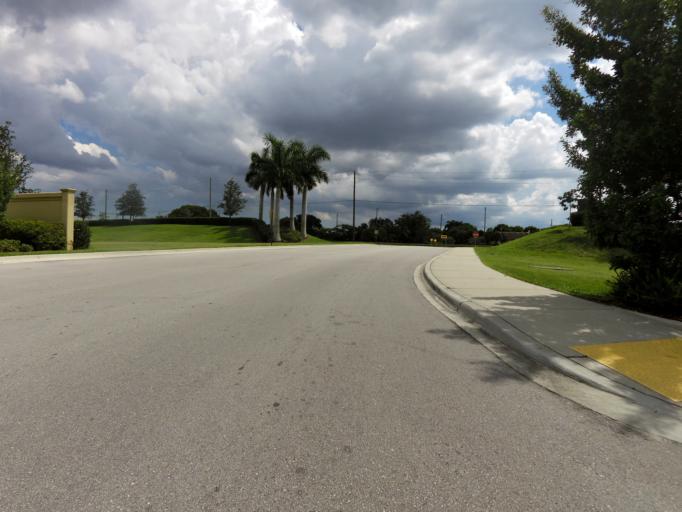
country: US
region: Florida
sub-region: Broward County
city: Cooper City
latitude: 26.0660
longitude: -80.2554
